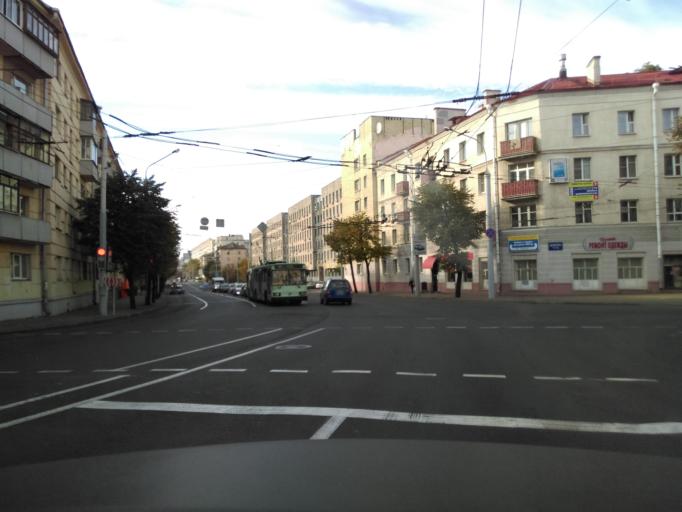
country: BY
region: Minsk
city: Minsk
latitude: 53.9244
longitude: 27.5991
